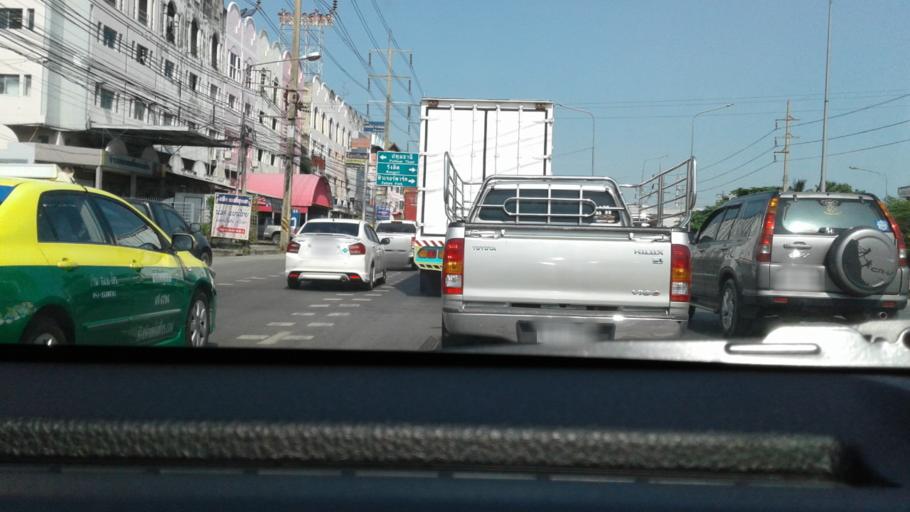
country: TH
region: Phra Nakhon Si Ayutthaya
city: Ban Bang Kadi Pathum Thani
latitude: 13.9818
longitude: 100.5930
